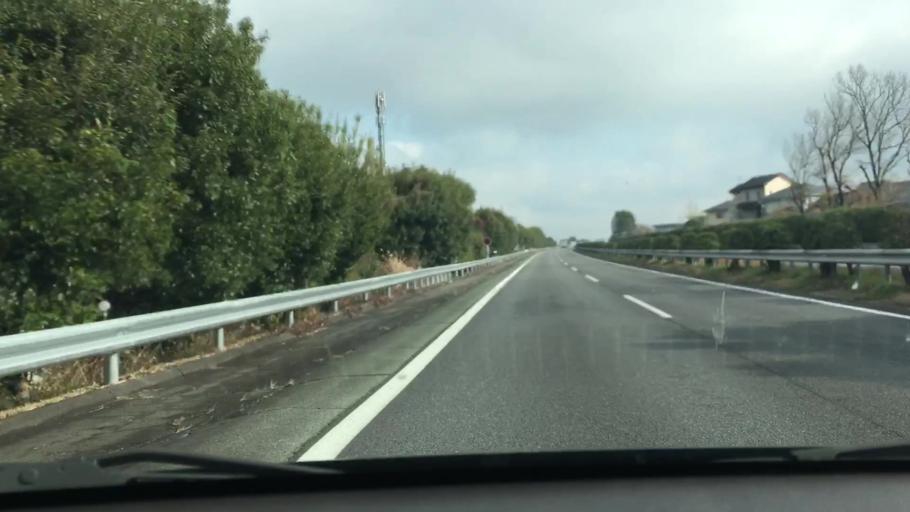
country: JP
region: Kumamoto
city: Kumamoto
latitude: 32.8565
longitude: 130.7544
